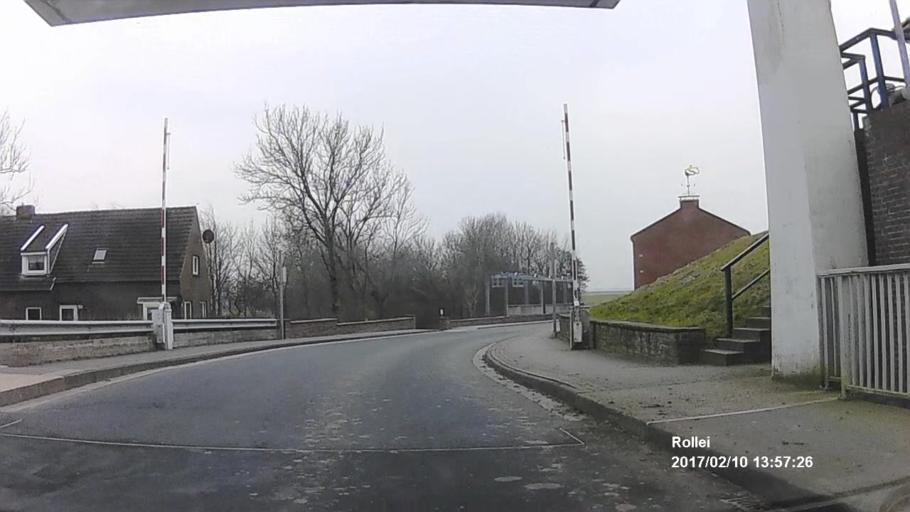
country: DE
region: Lower Saxony
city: Norddeich
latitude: 53.5424
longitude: 7.1432
